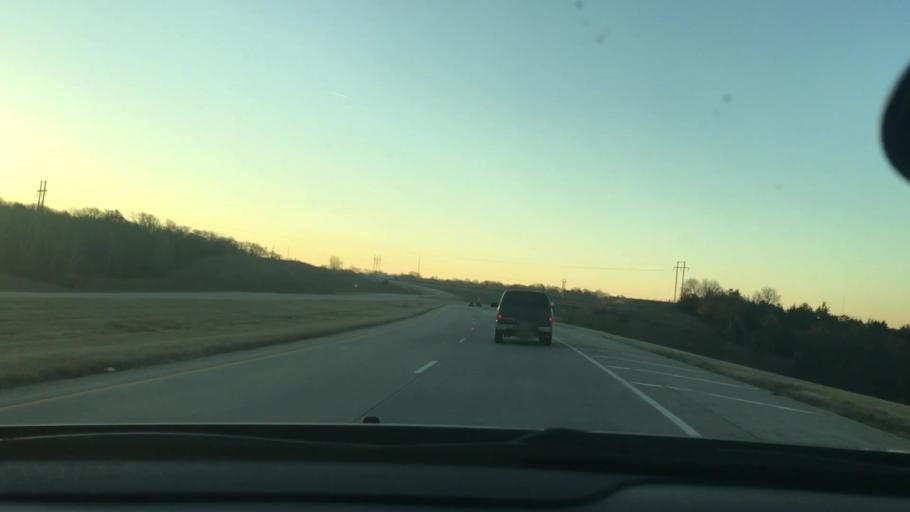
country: US
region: Oklahoma
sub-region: Pontotoc County
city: Ada
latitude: 34.7955
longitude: -96.6954
